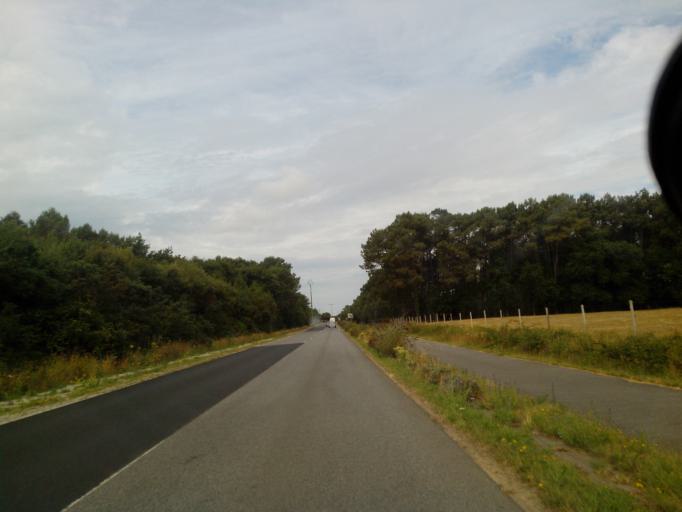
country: FR
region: Brittany
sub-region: Departement du Morbihan
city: Ploemel
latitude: 47.6427
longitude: -3.1045
